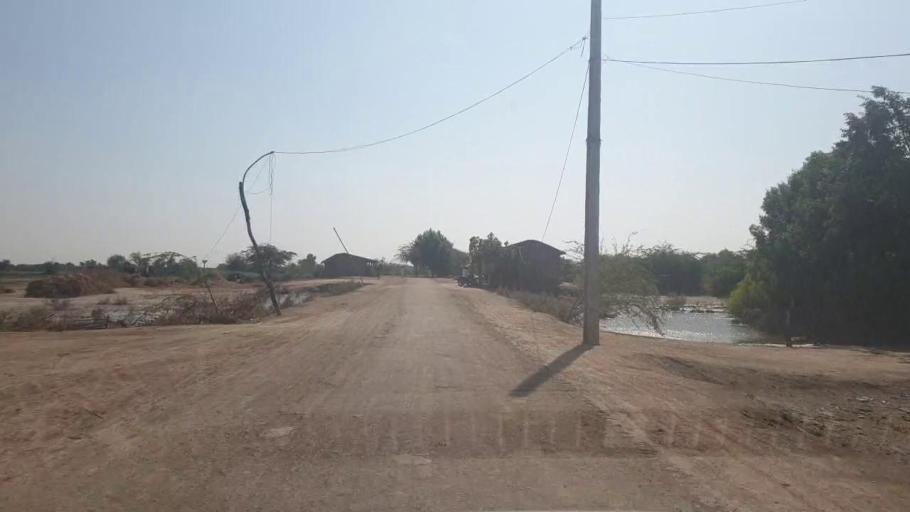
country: PK
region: Sindh
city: Badin
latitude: 24.5912
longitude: 68.8455
